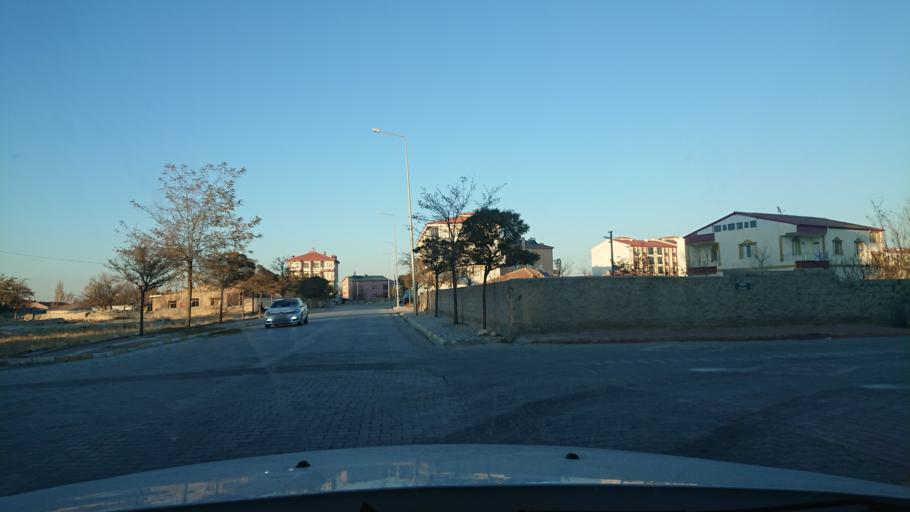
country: TR
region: Aksaray
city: Eskil
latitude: 38.4004
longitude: 33.4065
